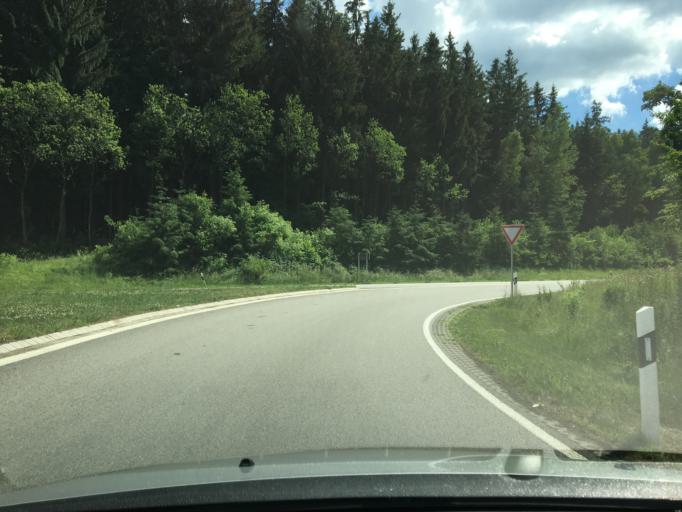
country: DE
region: Bavaria
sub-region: Lower Bavaria
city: Furth
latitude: 48.4298
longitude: 12.3859
